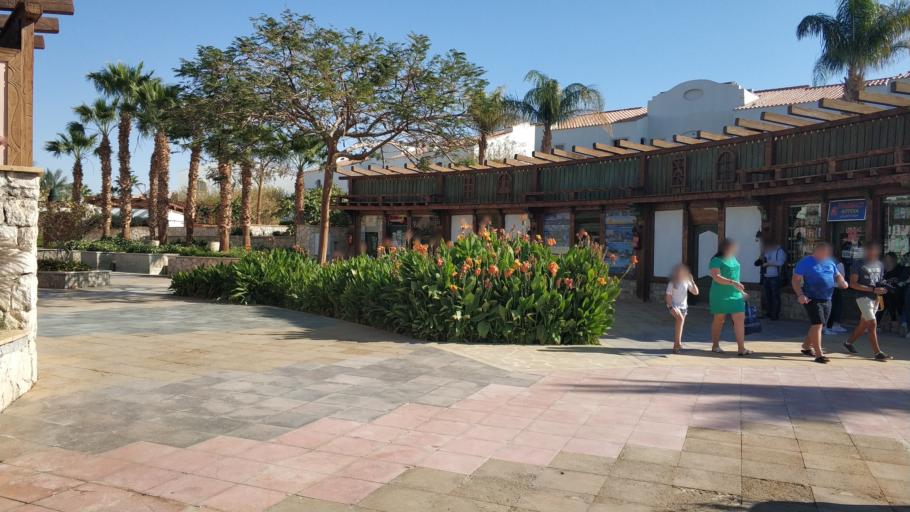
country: EG
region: South Sinai
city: Sharm el-Sheikh
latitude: 27.9170
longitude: 34.3613
